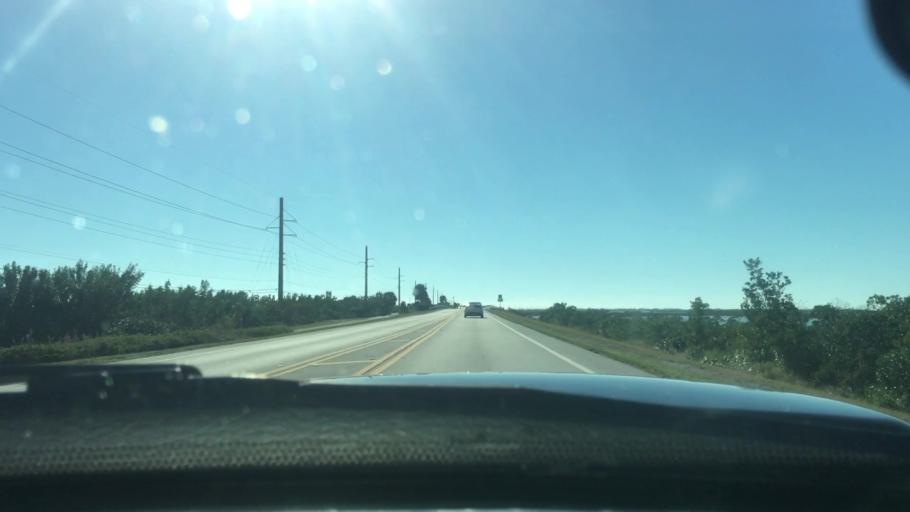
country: US
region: Florida
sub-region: Monroe County
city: Big Coppitt Key
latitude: 24.6278
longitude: -81.5952
